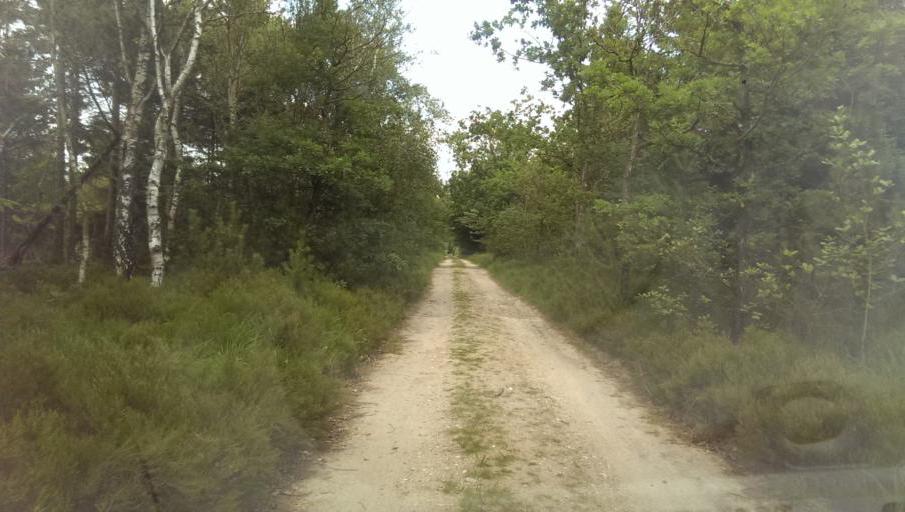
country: DK
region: South Denmark
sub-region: Varde Kommune
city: Varde
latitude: 55.5936
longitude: 8.5160
